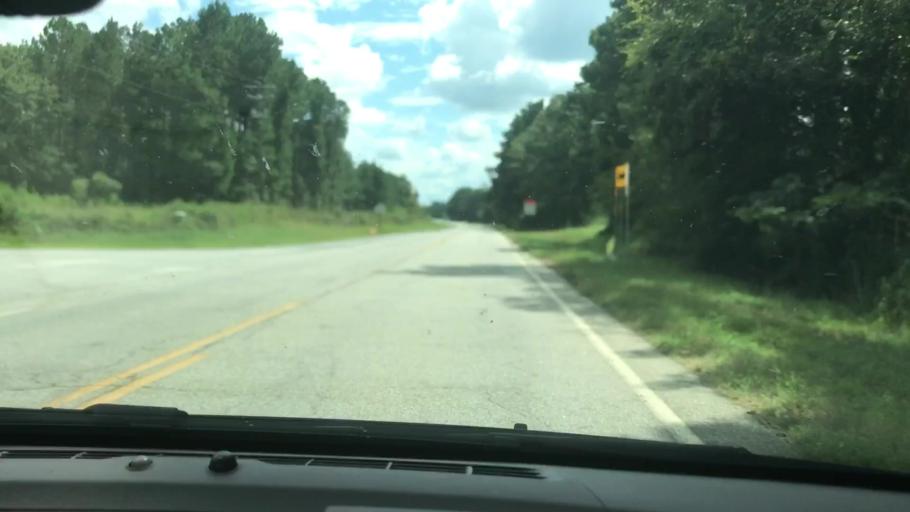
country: US
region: Georgia
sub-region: Clay County
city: Fort Gaines
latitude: 31.6698
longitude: -85.0466
